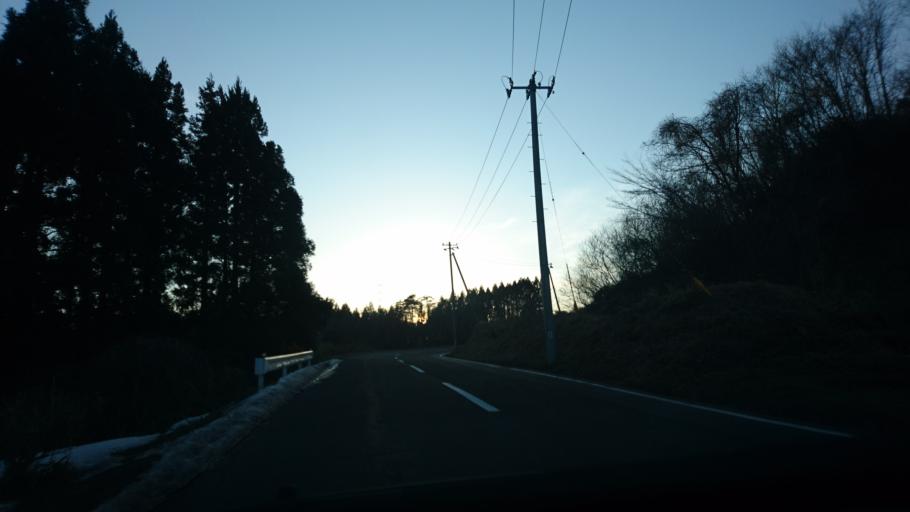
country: JP
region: Iwate
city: Mizusawa
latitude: 39.0392
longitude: 141.3184
